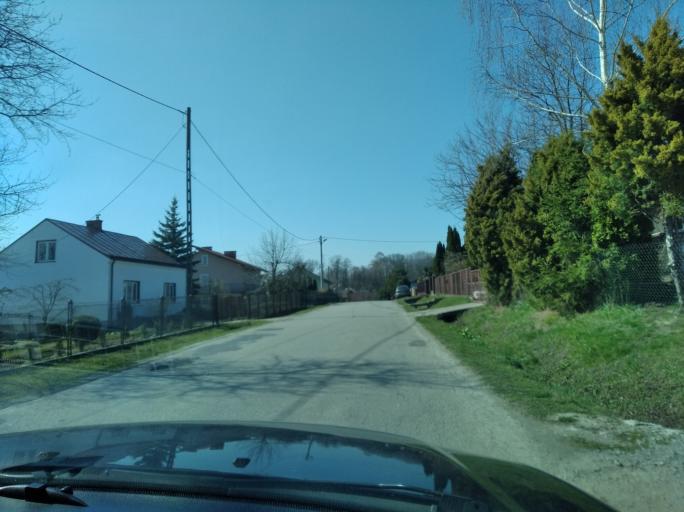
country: PL
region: Subcarpathian Voivodeship
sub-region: Powiat jaroslawski
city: Pruchnik
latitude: 49.9326
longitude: 22.4980
